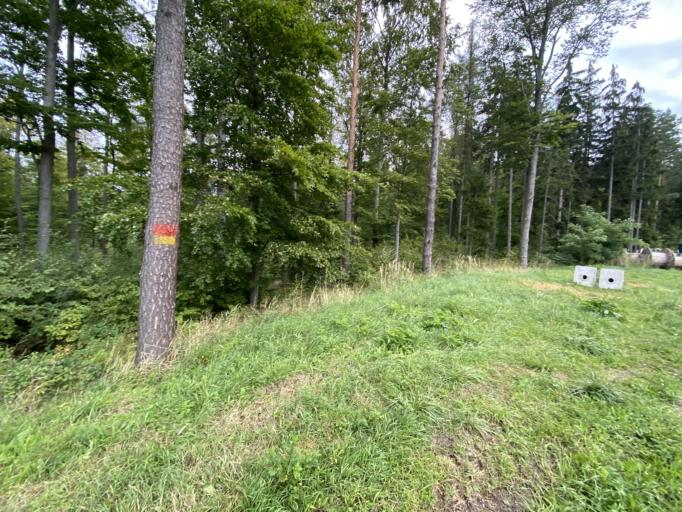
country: AT
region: Lower Austria
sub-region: Politischer Bezirk Wiener Neustadt
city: Wiesmath
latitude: 47.5713
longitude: 16.3293
